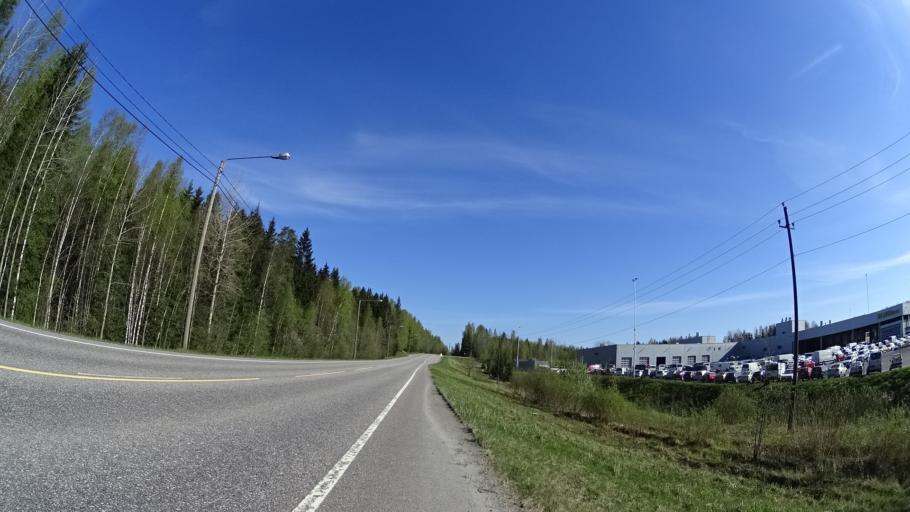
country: FI
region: Uusimaa
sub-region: Helsinki
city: Nurmijaervi
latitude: 60.3699
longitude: 24.8054
